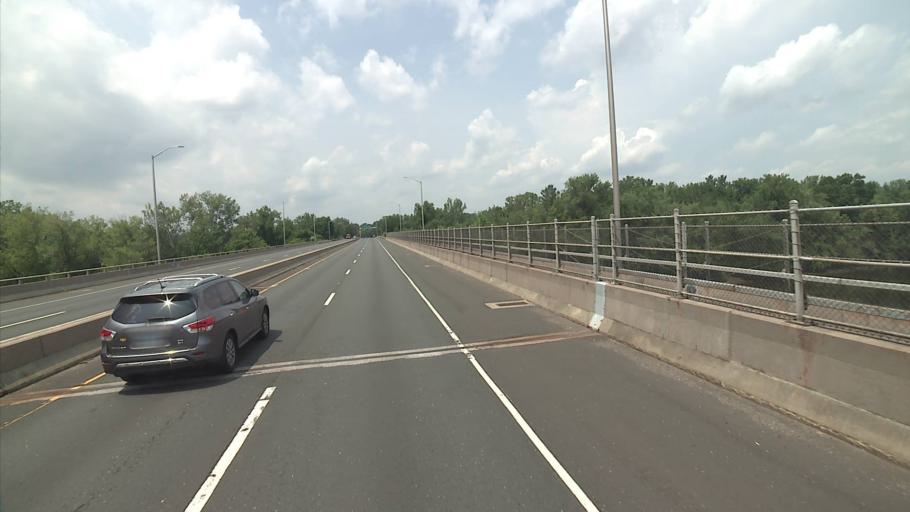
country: US
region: Connecticut
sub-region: Hartford County
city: South Windsor
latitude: 41.8134
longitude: -72.6454
